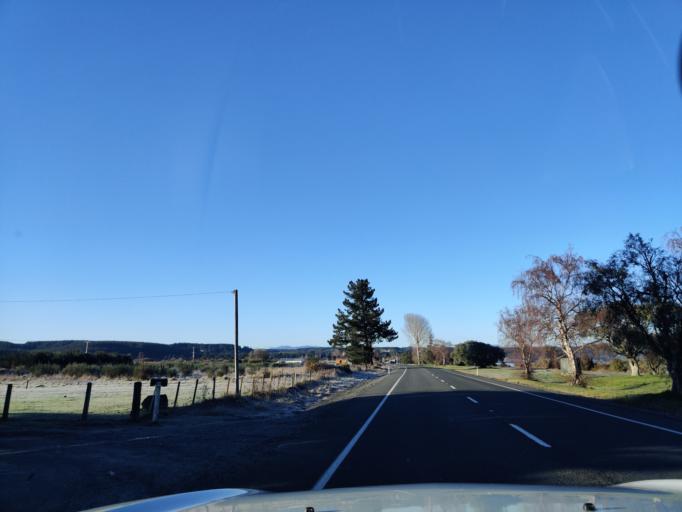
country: NZ
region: Waikato
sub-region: Taupo District
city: Taupo
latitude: -38.7735
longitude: 176.0764
